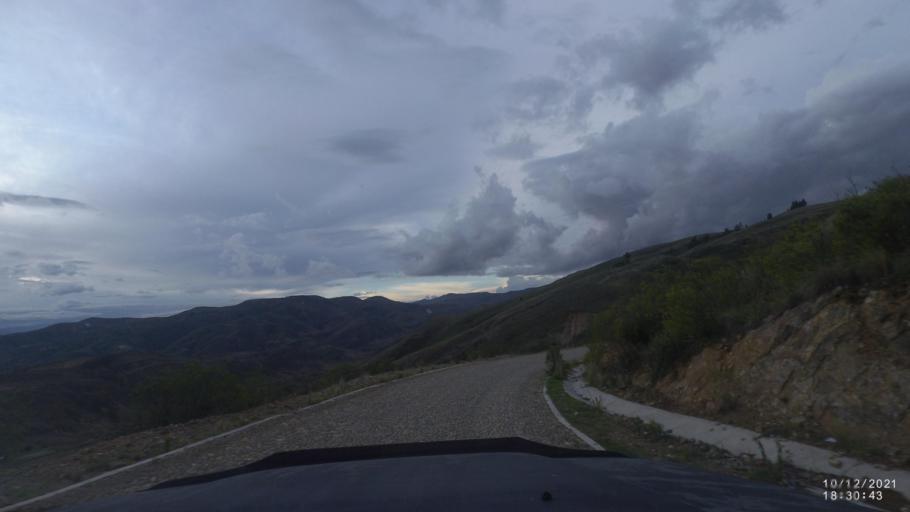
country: BO
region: Cochabamba
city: Tarata
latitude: -17.8155
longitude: -65.9832
